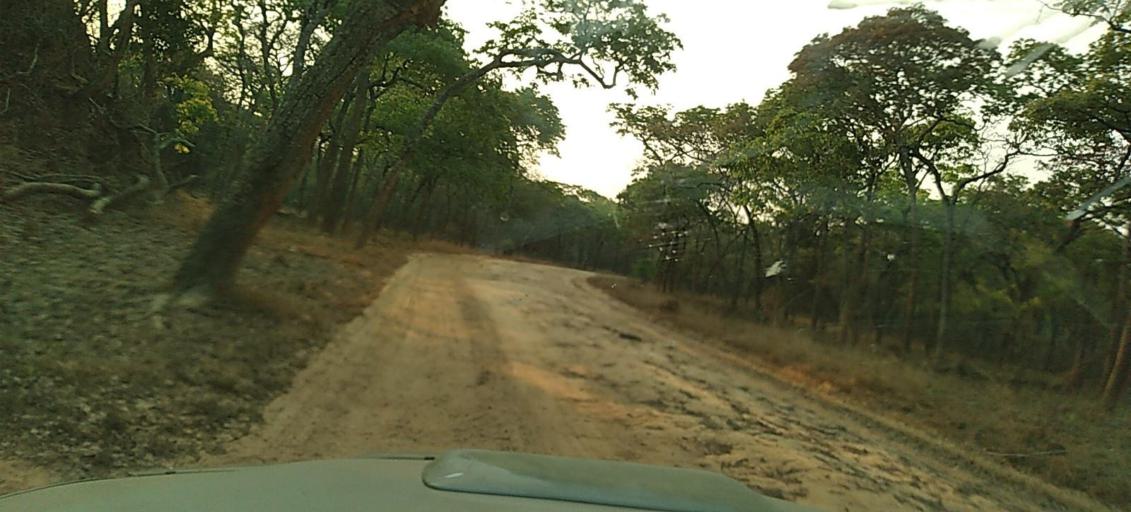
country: ZM
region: North-Western
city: Kasempa
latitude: -13.1553
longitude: 26.4438
